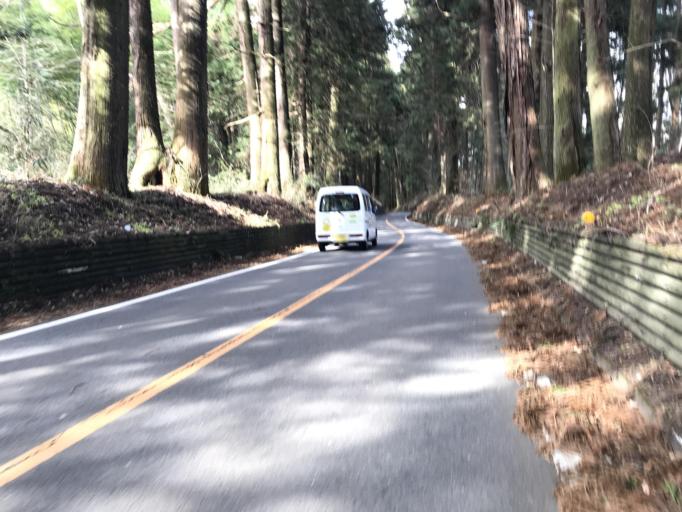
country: JP
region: Tochigi
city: Imaichi
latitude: 36.6917
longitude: 139.7161
